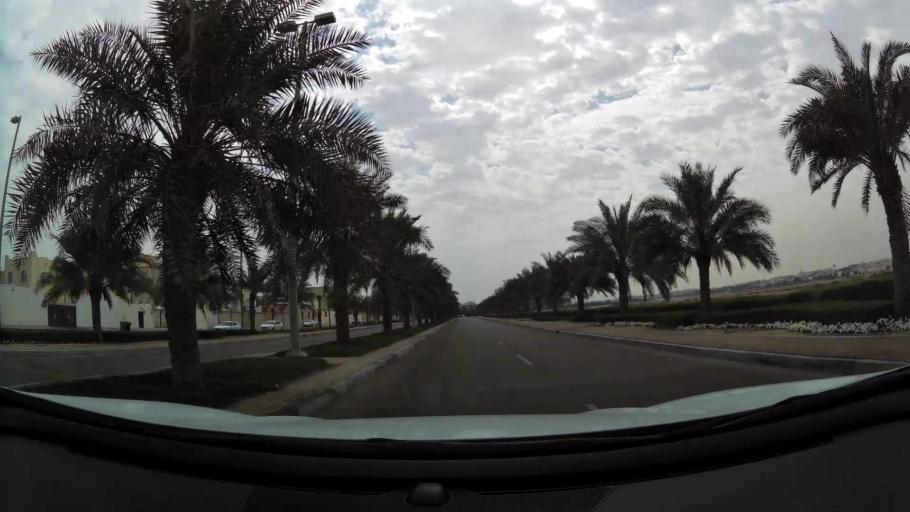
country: AE
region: Abu Dhabi
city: Abu Dhabi
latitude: 24.3174
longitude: 54.6144
